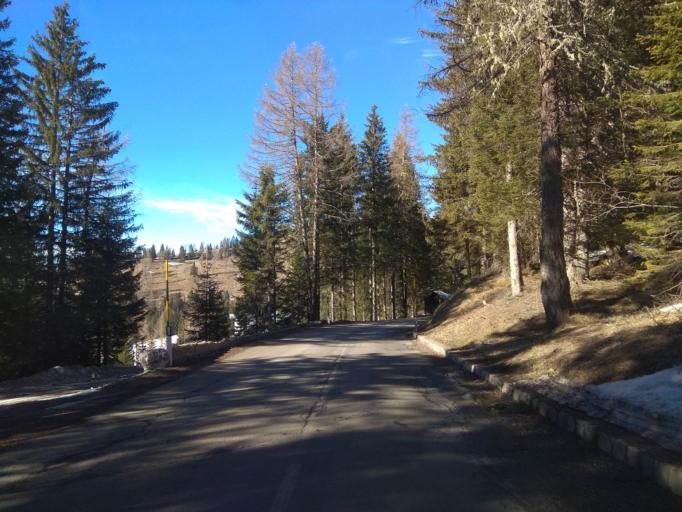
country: IT
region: Trentino-Alto Adige
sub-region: Bolzano
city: Nova Levante
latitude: 46.4289
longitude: 11.5987
